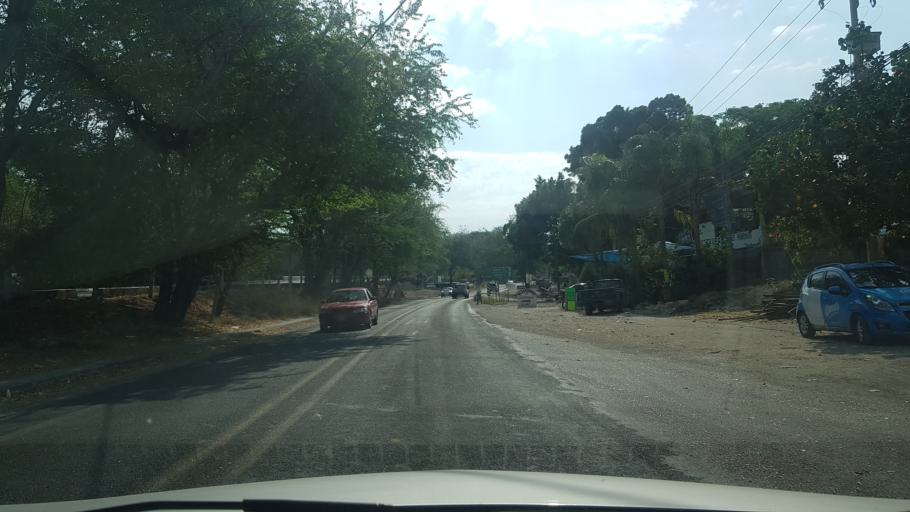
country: MX
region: Morelos
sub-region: Amacuzac
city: San Gabriel las Palmas
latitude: 18.6122
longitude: -99.3459
